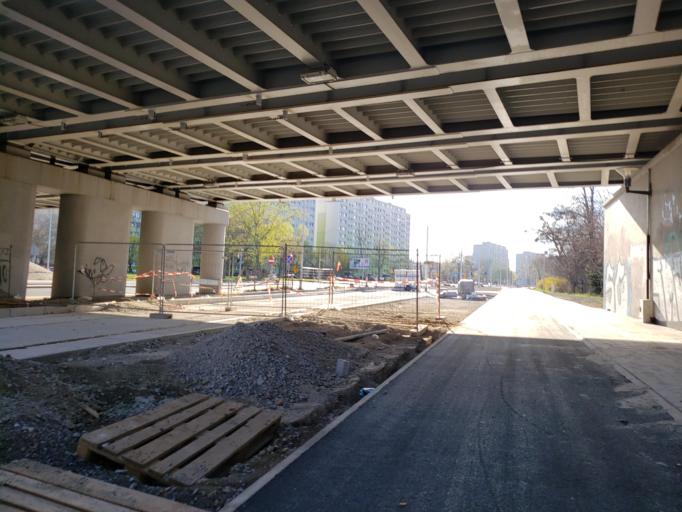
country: PL
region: Lower Silesian Voivodeship
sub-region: Powiat wroclawski
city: Wroclaw
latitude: 51.1263
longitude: 17.0013
